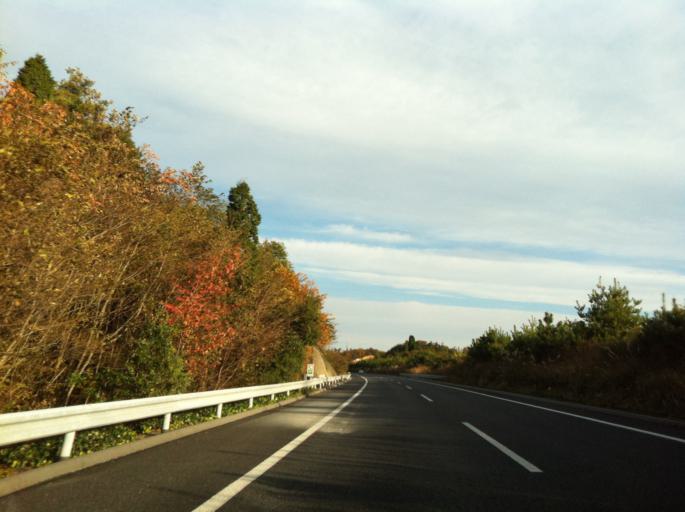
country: JP
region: Gifu
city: Tajimi
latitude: 35.2986
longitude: 137.1806
